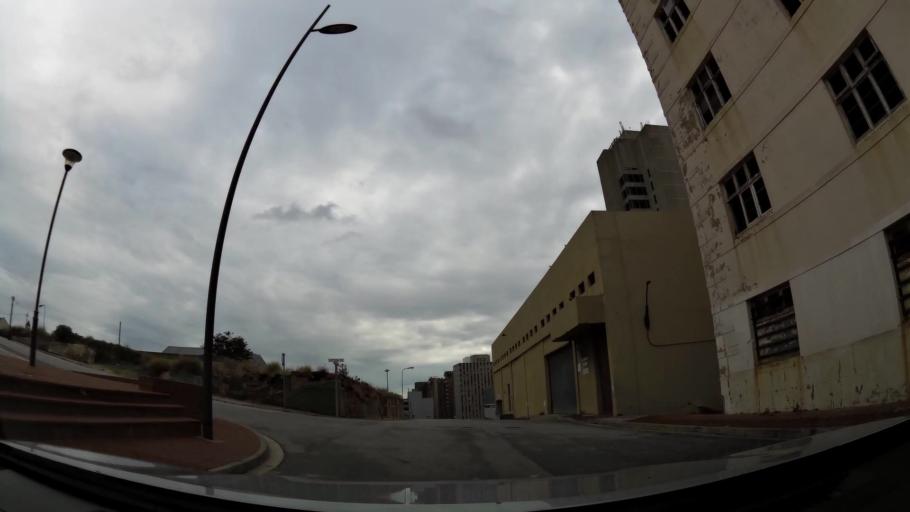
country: ZA
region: Eastern Cape
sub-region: Nelson Mandela Bay Metropolitan Municipality
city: Port Elizabeth
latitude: -33.9596
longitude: 25.6196
